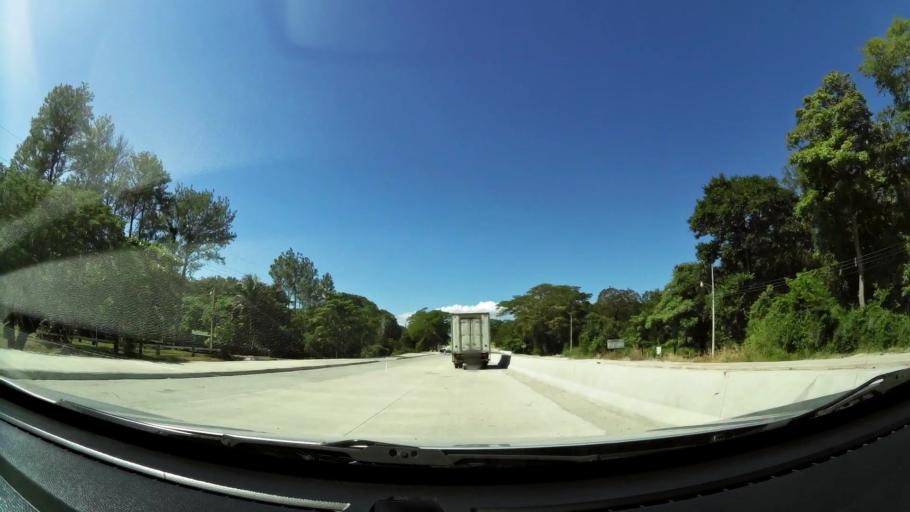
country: CR
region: Guanacaste
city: Liberia
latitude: 10.5786
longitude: -85.4050
